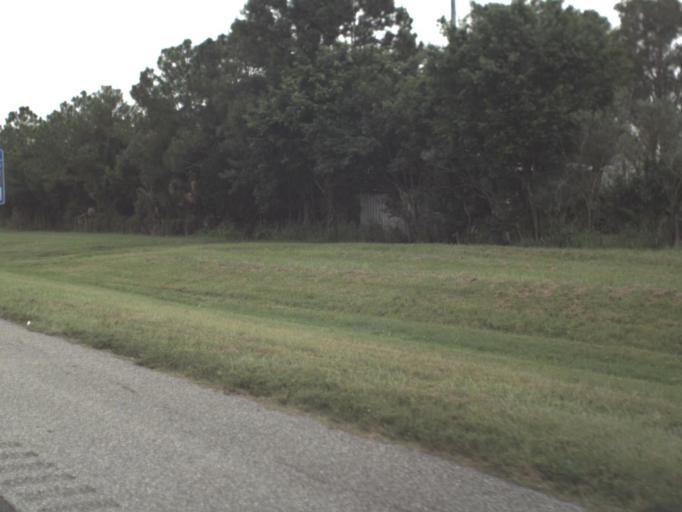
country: US
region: Florida
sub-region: Manatee County
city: Memphis
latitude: 27.5845
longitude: -82.5560
